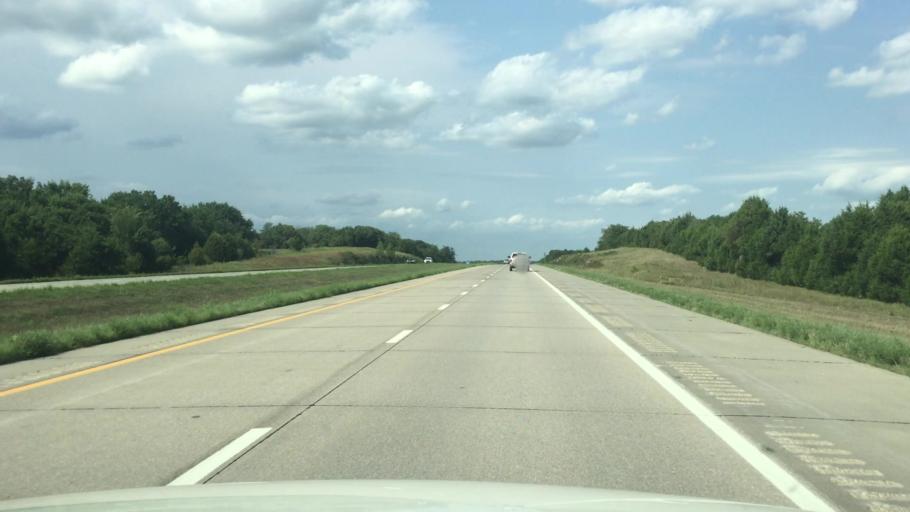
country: US
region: Kansas
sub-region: Miami County
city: Louisburg
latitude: 38.5811
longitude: -94.6952
